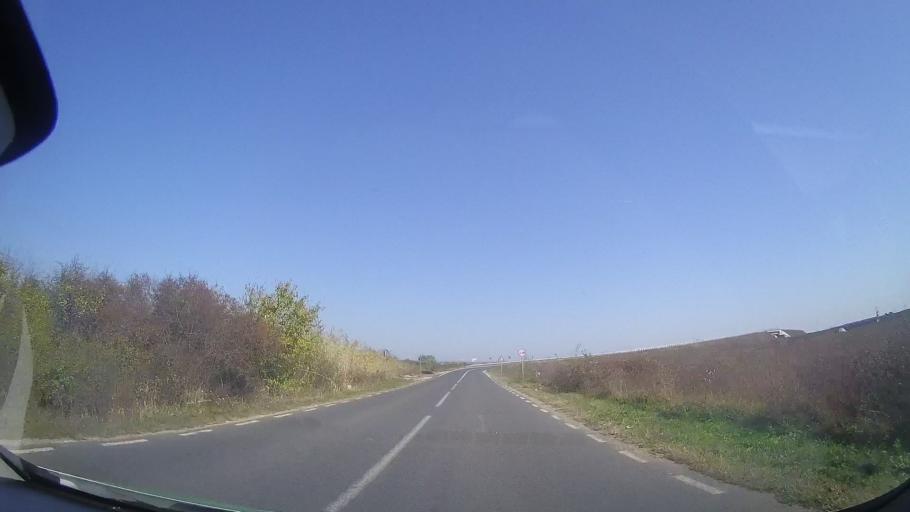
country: RO
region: Timis
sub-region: Comuna Balint
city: Balint
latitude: 45.7863
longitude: 21.8483
